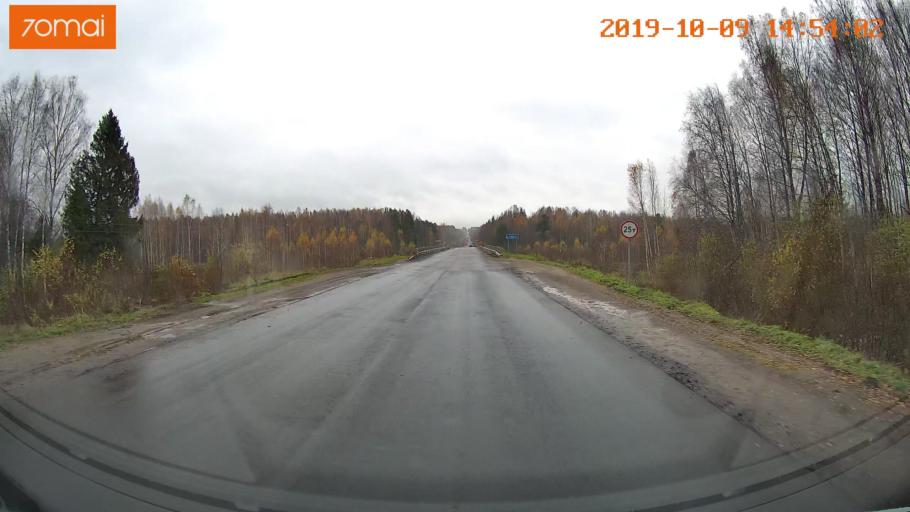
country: RU
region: Kostroma
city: Chistyye Bory
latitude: 58.3607
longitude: 41.6412
